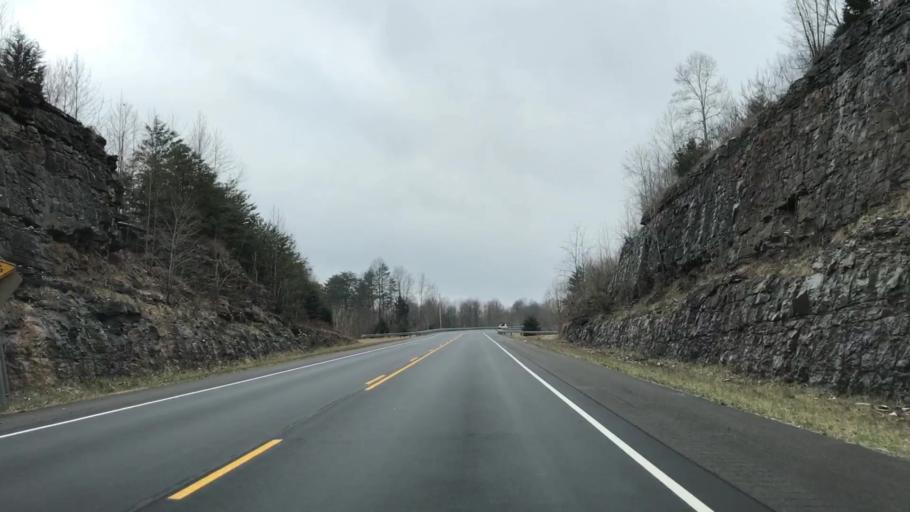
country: US
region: Kentucky
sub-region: Adair County
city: Columbia
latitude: 36.9758
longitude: -85.4200
